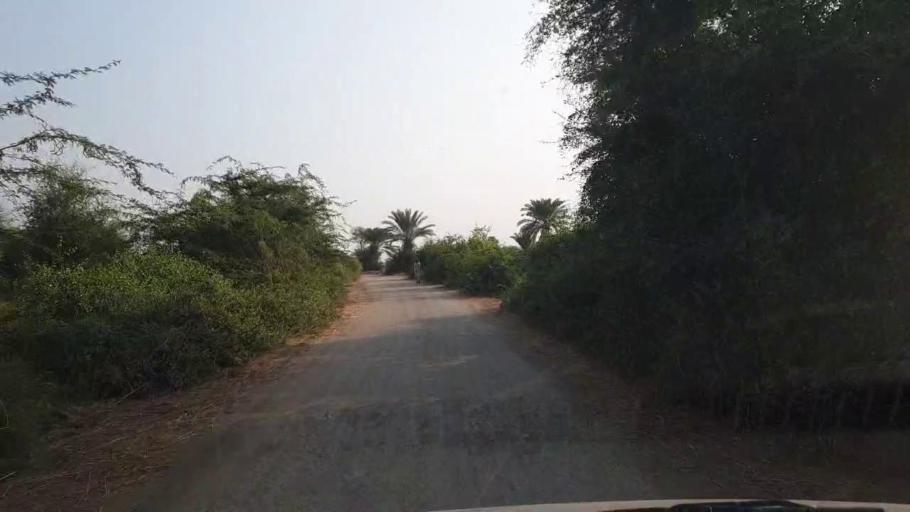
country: PK
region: Sindh
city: Matli
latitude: 25.0628
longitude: 68.7604
